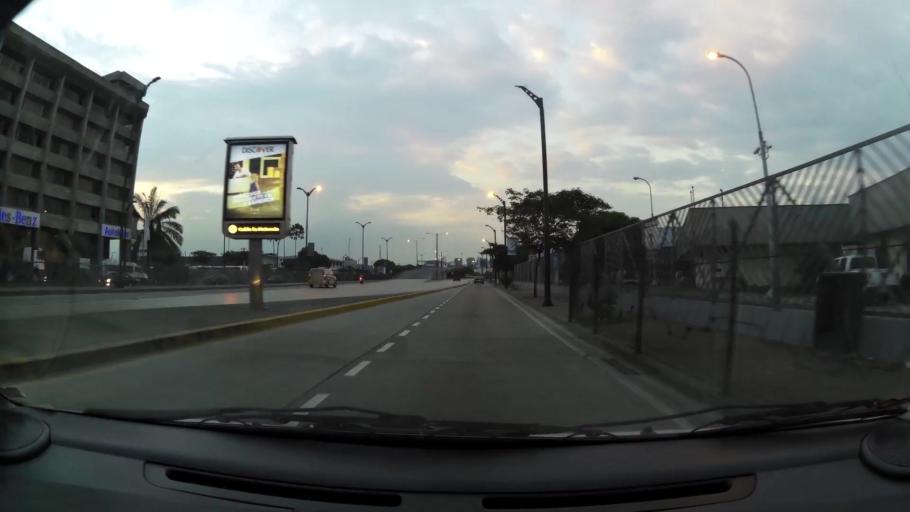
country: EC
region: Guayas
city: Eloy Alfaro
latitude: -2.1666
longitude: -79.8919
